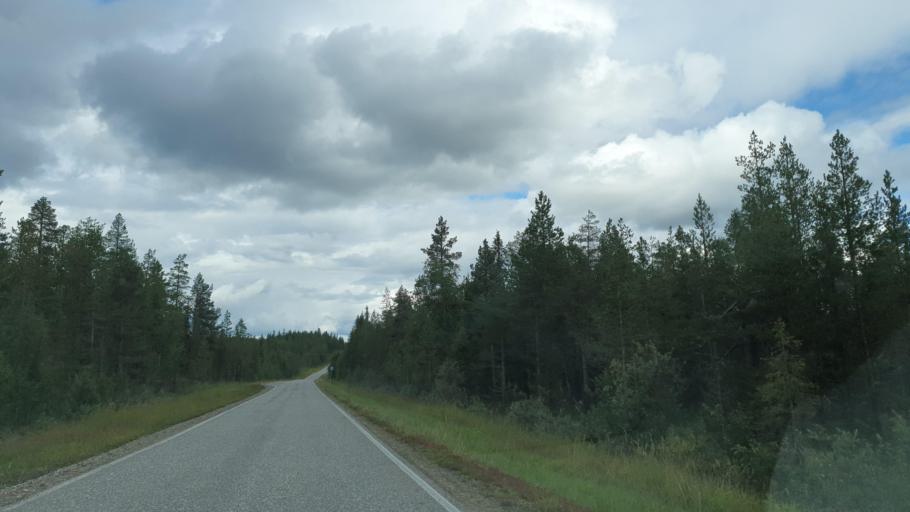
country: FI
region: Lapland
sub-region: Tunturi-Lappi
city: Muonio
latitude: 67.8259
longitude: 24.0720
